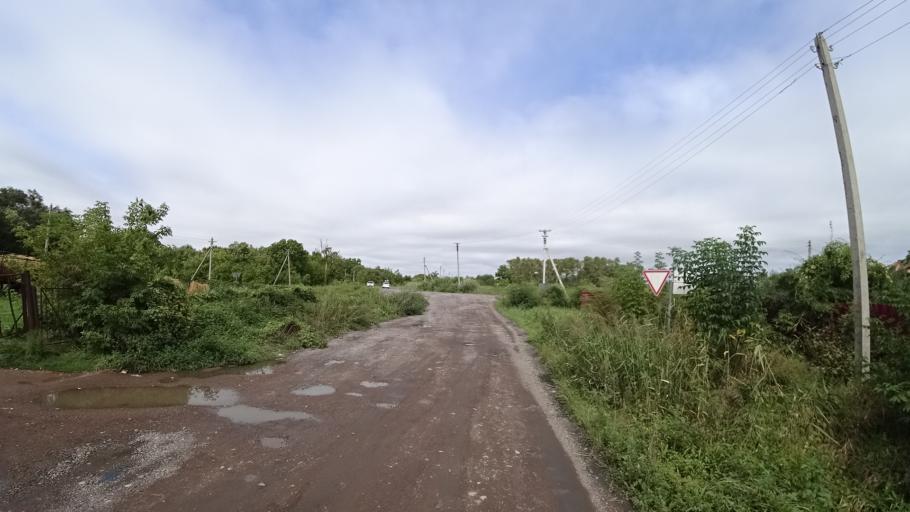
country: RU
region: Primorskiy
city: Monastyrishche
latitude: 44.1896
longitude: 132.4823
